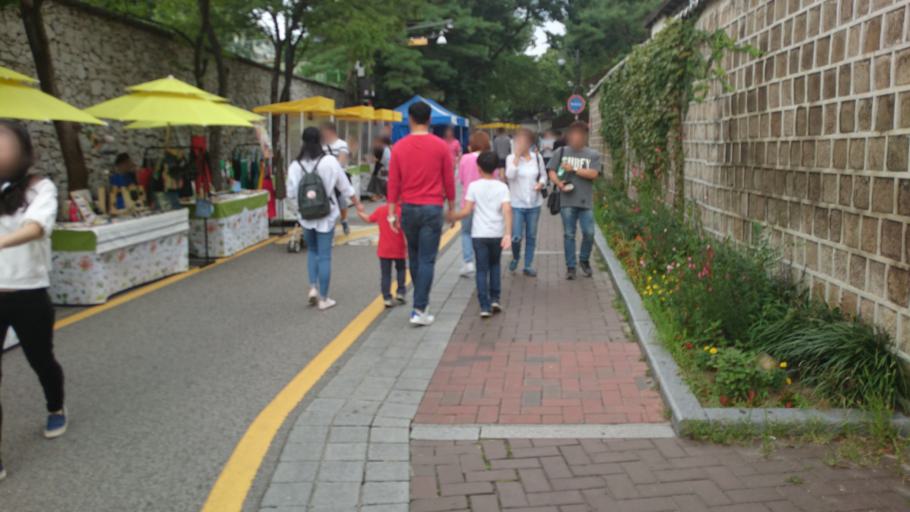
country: KR
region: Seoul
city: Seoul
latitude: 37.5771
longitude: 126.9825
